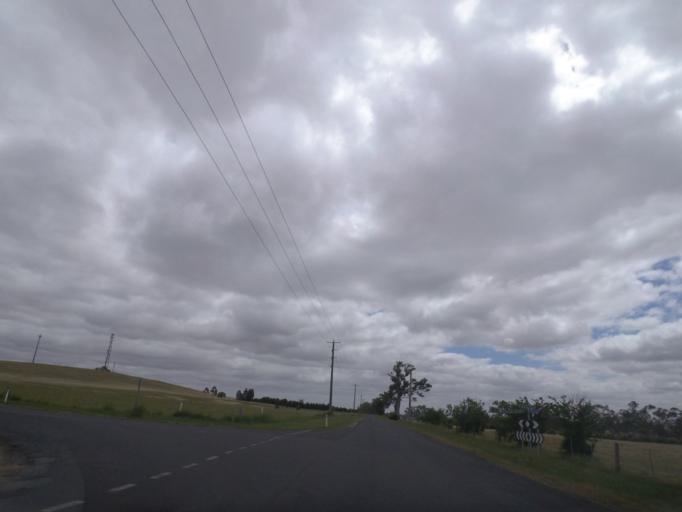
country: AU
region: Victoria
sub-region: Whittlesea
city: Whittlesea
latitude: -37.1860
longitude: 145.0380
